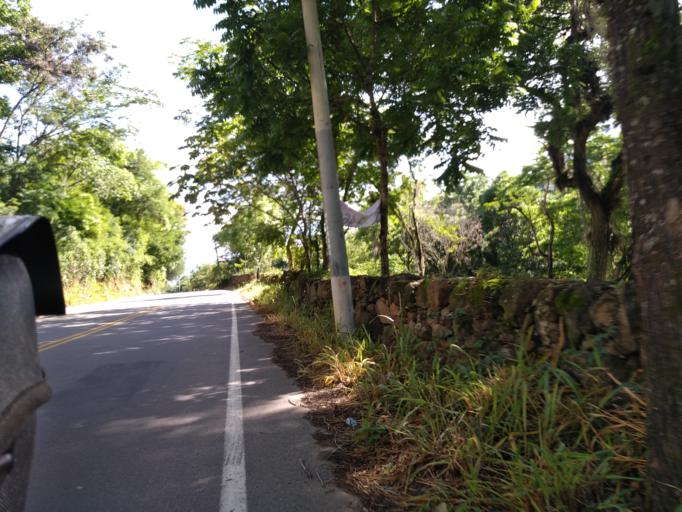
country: CO
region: Santander
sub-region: San Gil
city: San Gil
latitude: 6.5243
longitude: -73.1252
